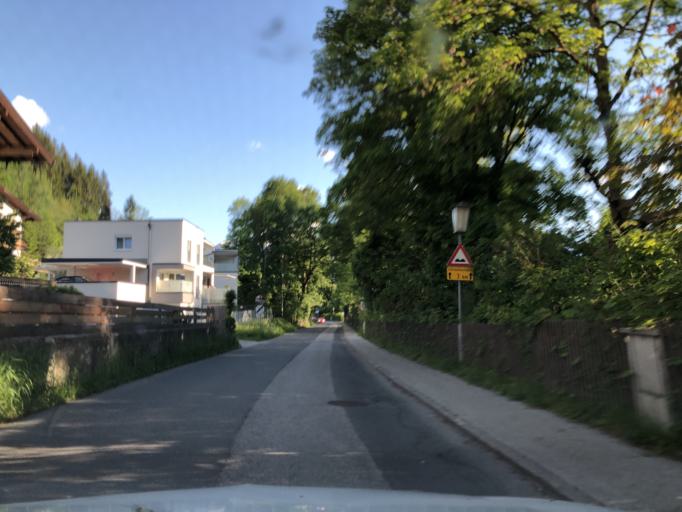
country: AT
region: Salzburg
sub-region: Politischer Bezirk Zell am See
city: Zell am See
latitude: 47.3272
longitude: 12.8166
